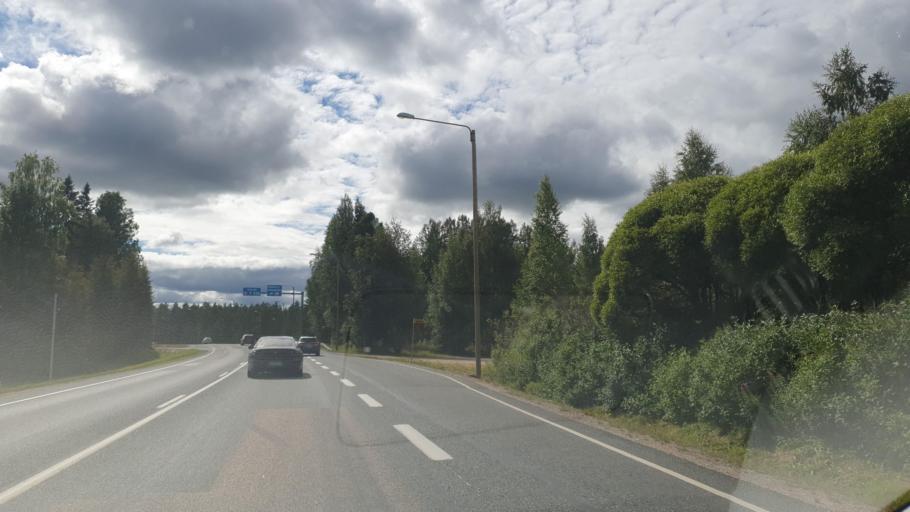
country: FI
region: Kainuu
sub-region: Kajaani
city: Kajaani
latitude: 64.1199
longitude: 27.4543
